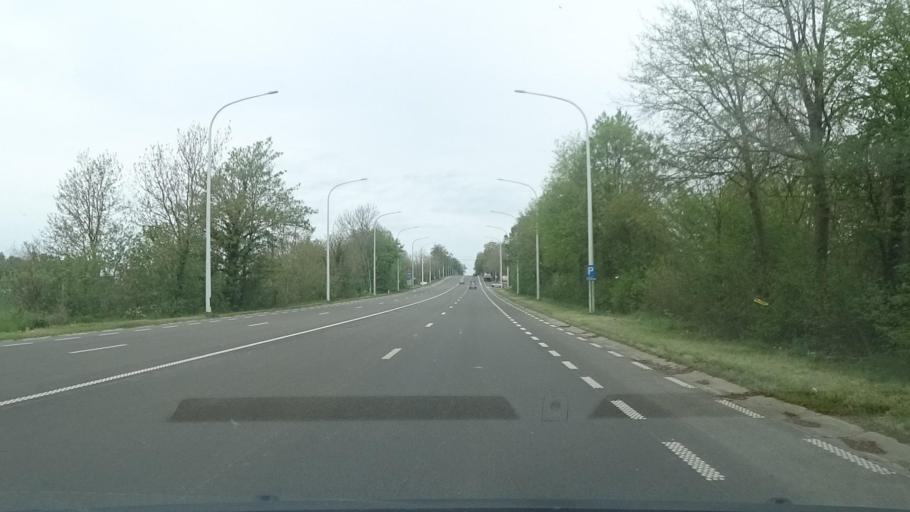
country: BE
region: Wallonia
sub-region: Province de Namur
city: Floreffe
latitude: 50.5012
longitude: 4.7820
